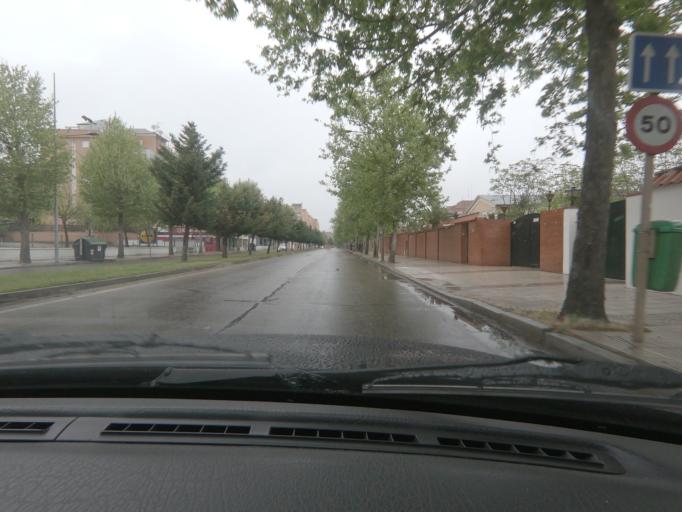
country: ES
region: Extremadura
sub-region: Provincia de Badajoz
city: Badajoz
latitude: 38.8636
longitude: -6.9724
